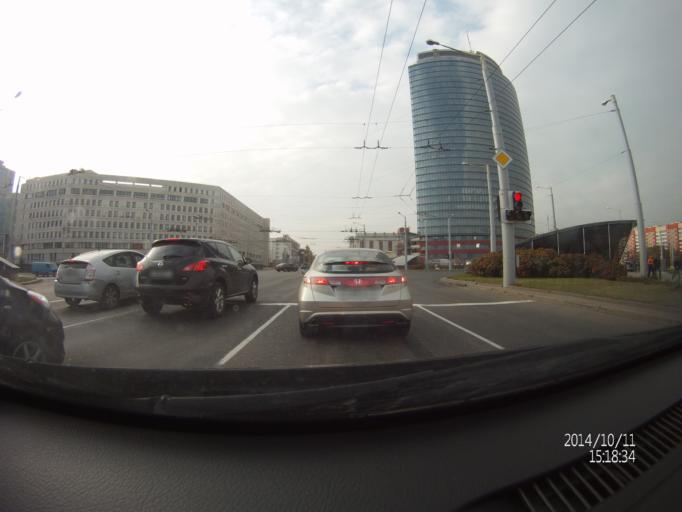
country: BY
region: Minsk
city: Minsk
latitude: 53.9061
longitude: 27.5343
